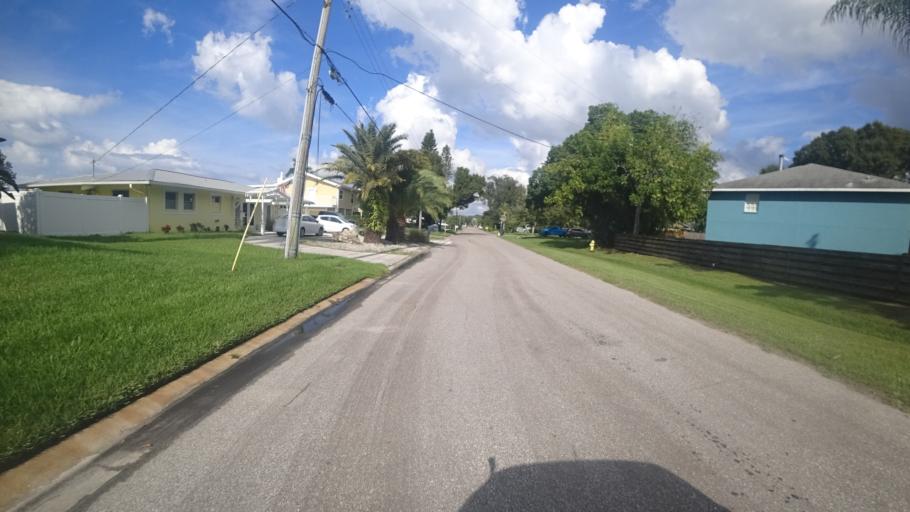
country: US
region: Florida
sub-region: Manatee County
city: Memphis
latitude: 27.5613
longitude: -82.5677
